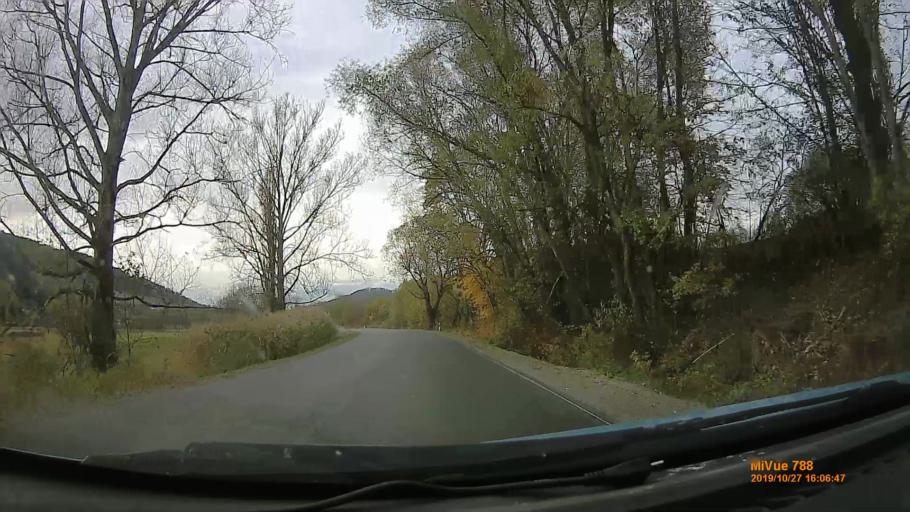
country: PL
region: Lower Silesian Voivodeship
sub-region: Powiat klodzki
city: Nowa Ruda
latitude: 50.5408
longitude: 16.4677
